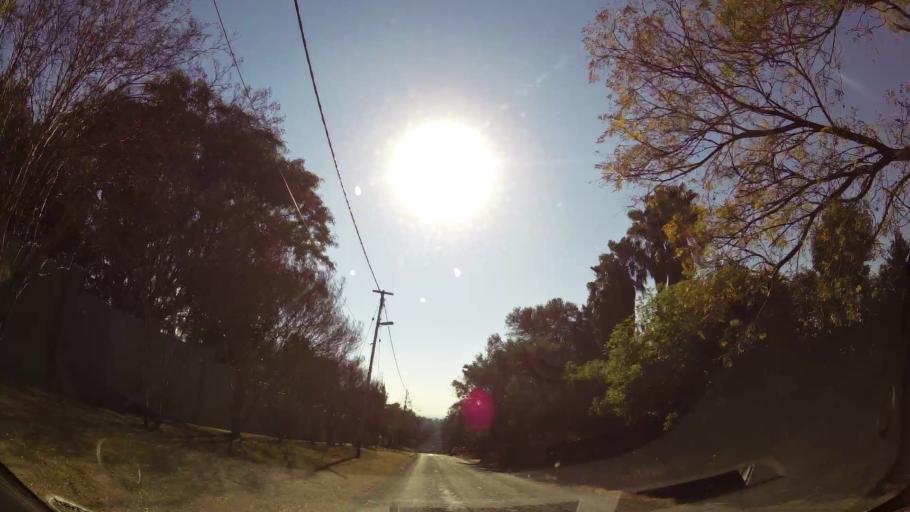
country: ZA
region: Gauteng
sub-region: City of Johannesburg Metropolitan Municipality
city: Midrand
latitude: -26.0524
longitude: 28.0483
